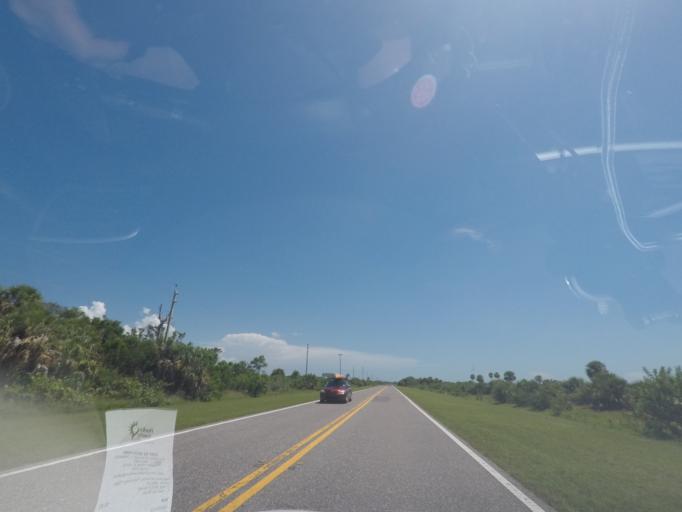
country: US
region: Florida
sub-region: Pinellas County
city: Tierra Verde
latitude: 27.6308
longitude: -82.7350
